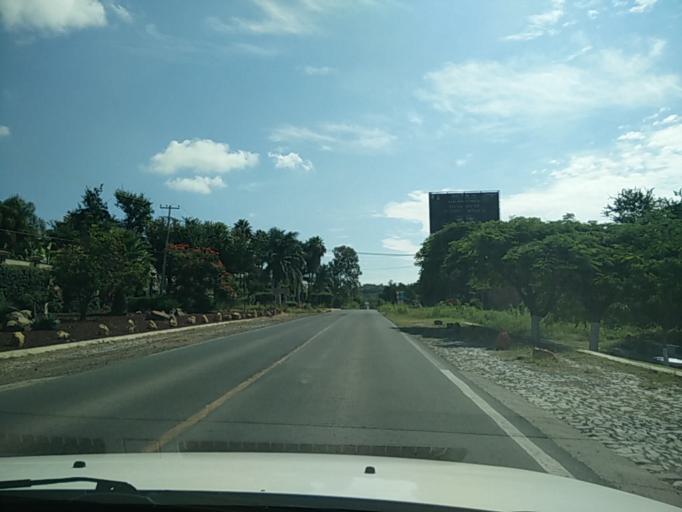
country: MX
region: Jalisco
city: Ajijic
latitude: 20.3024
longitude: -103.2380
